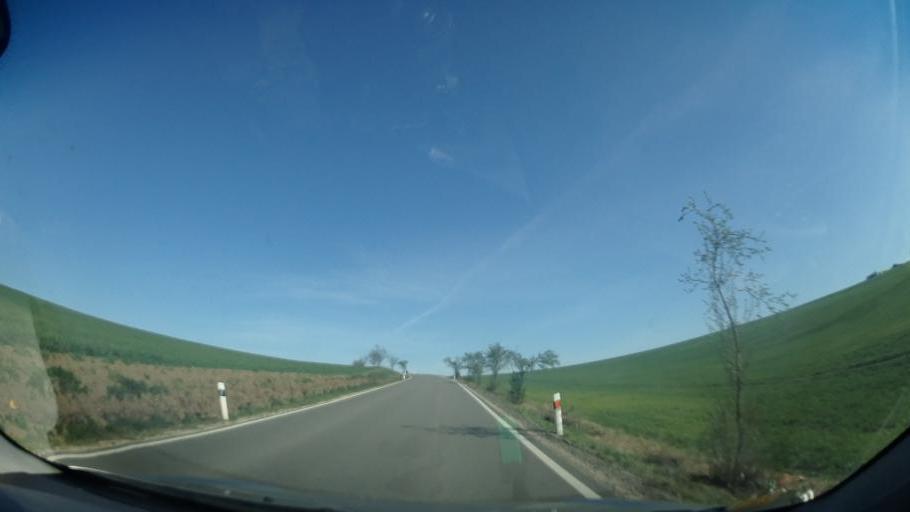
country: CZ
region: South Moravian
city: Moravany
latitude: 49.1500
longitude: 16.5632
